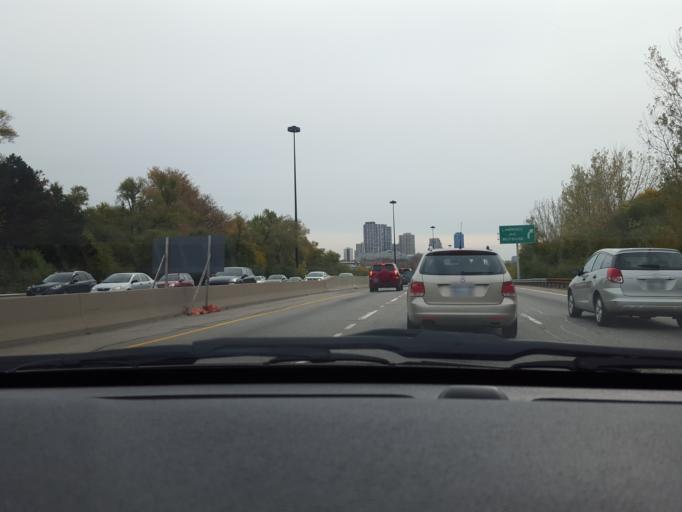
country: CA
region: Ontario
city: Willowdale
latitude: 43.7445
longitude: -79.3329
